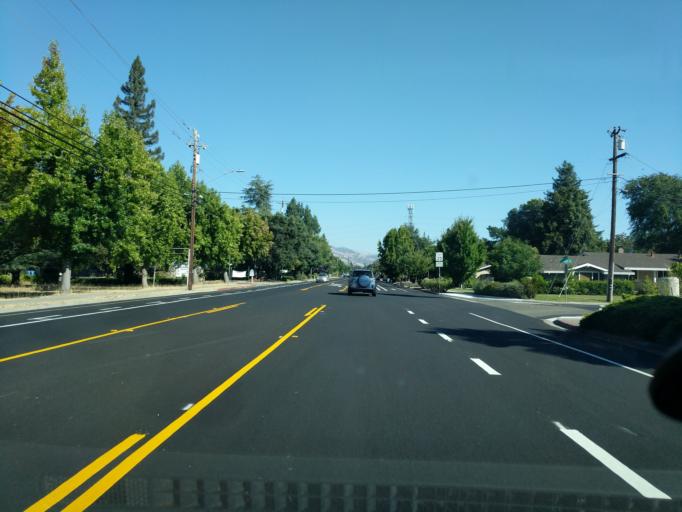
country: US
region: California
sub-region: Contra Costa County
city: Waldon
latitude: 37.9195
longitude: -122.0321
